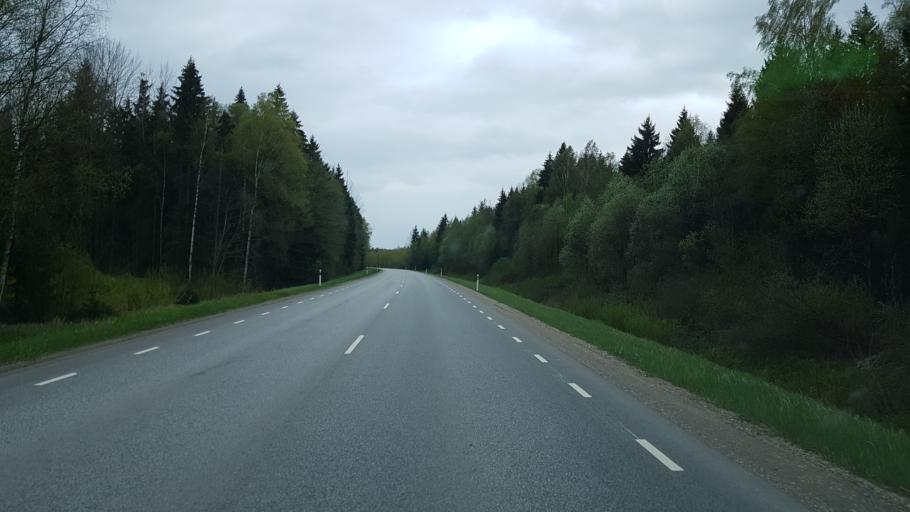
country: EE
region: Viljandimaa
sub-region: Vohma linn
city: Vohma
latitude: 58.5756
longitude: 25.5696
